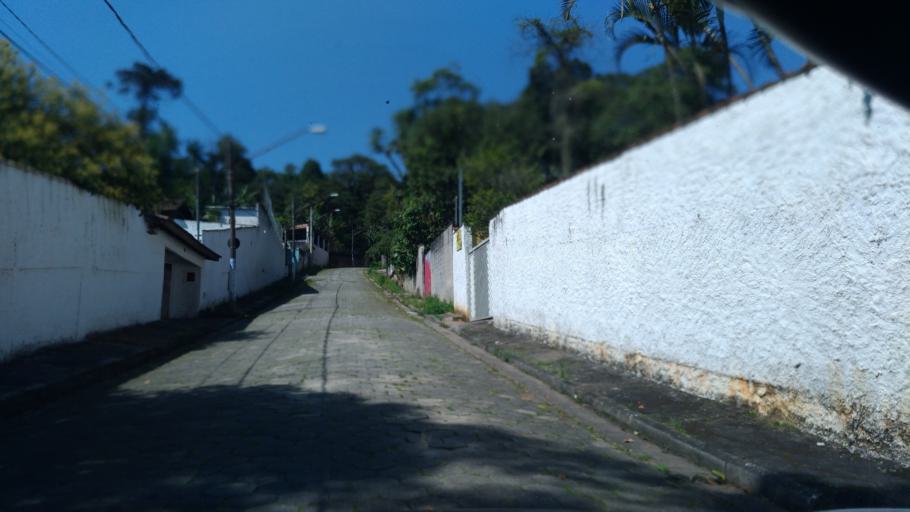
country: BR
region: Sao Paulo
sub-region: Sao Bernardo Do Campo
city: Sao Bernardo do Campo
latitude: -23.7720
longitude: -46.5207
